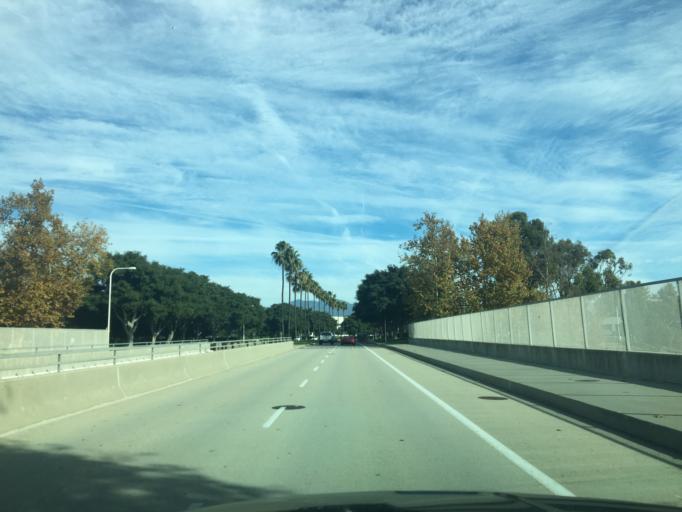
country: US
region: California
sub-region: Orange County
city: Irvine
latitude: 33.6572
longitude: -117.7651
